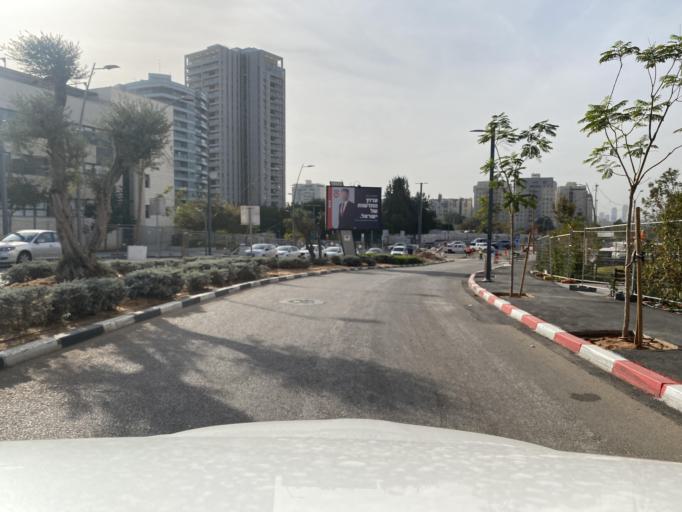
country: IL
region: Tel Aviv
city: Giv`at Shemu'el
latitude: 32.0702
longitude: 34.8514
